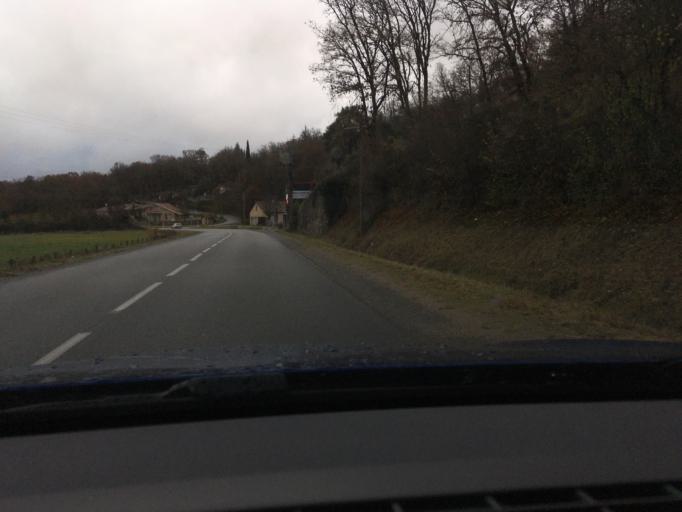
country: FR
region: Midi-Pyrenees
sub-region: Departement de l'Aveyron
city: Villefranche-de-Rouergue
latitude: 44.3693
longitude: 2.0159
